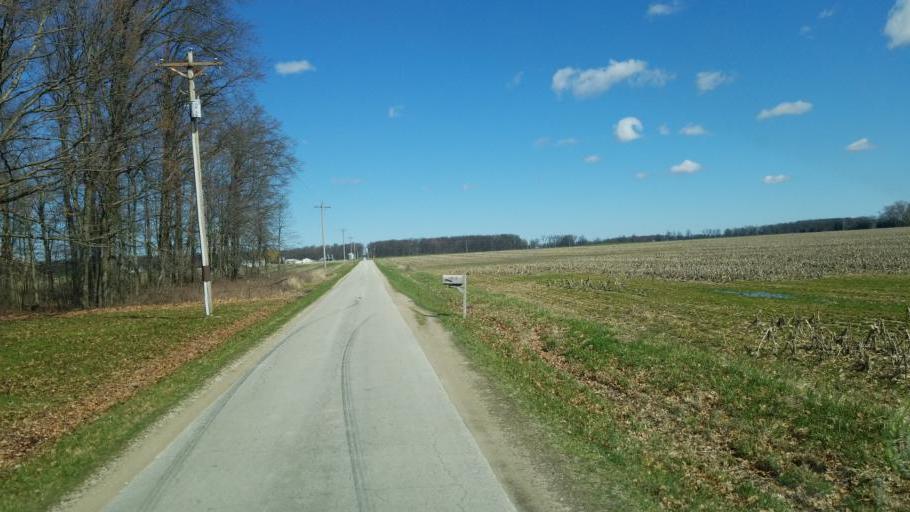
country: US
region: Ohio
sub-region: Sandusky County
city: Mount Carmel
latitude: 41.2368
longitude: -82.9369
